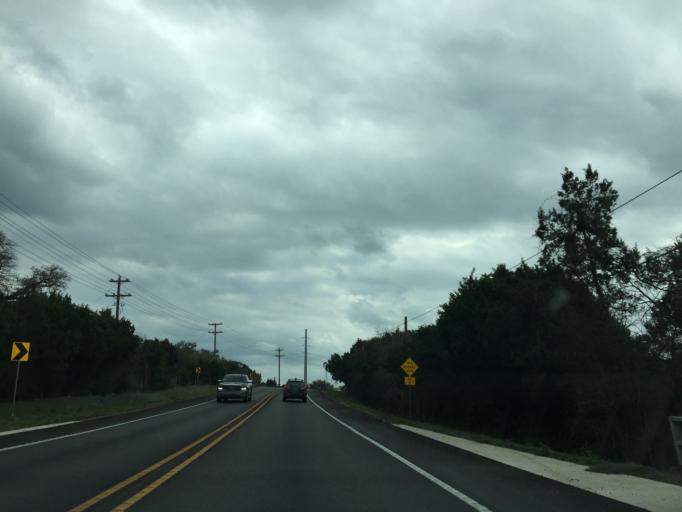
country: US
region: Texas
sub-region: Travis County
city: Shady Hollow
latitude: 30.1772
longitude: -97.9289
